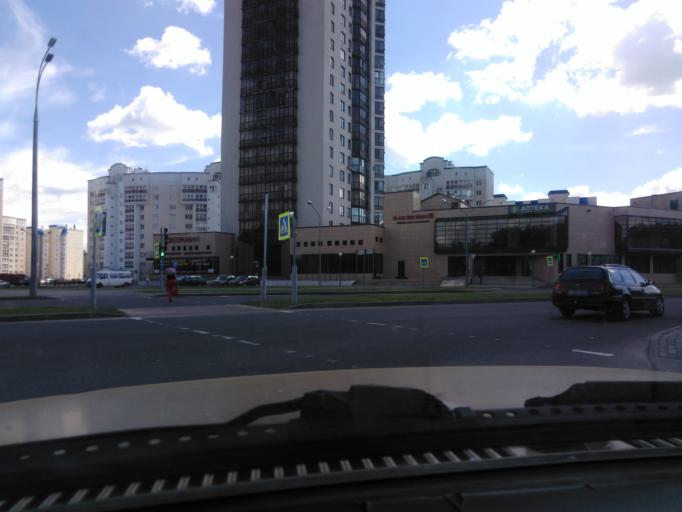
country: BY
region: Mogilev
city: Mahilyow
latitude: 53.9202
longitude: 30.2863
